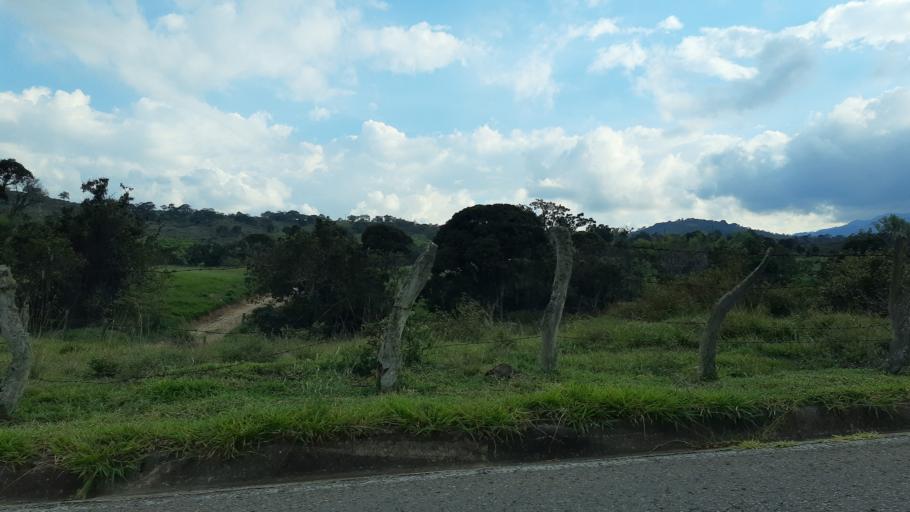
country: CO
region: Boyaca
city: Moniquira
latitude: 5.8262
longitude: -73.5924
